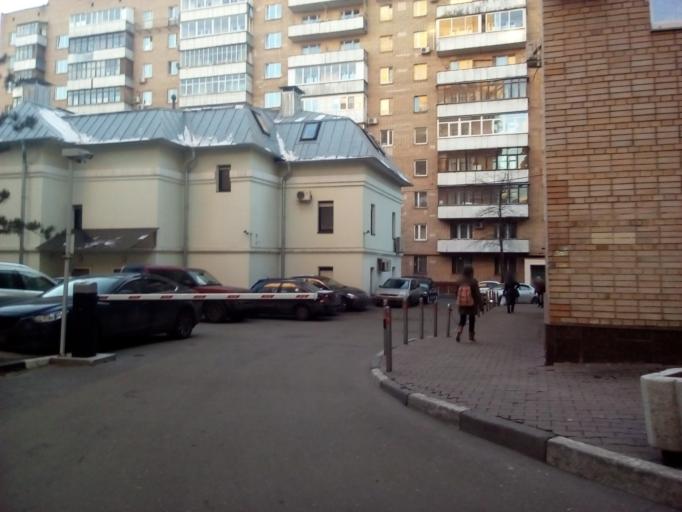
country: RU
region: Moskovskaya
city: Dorogomilovo
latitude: 55.7654
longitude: 37.5807
